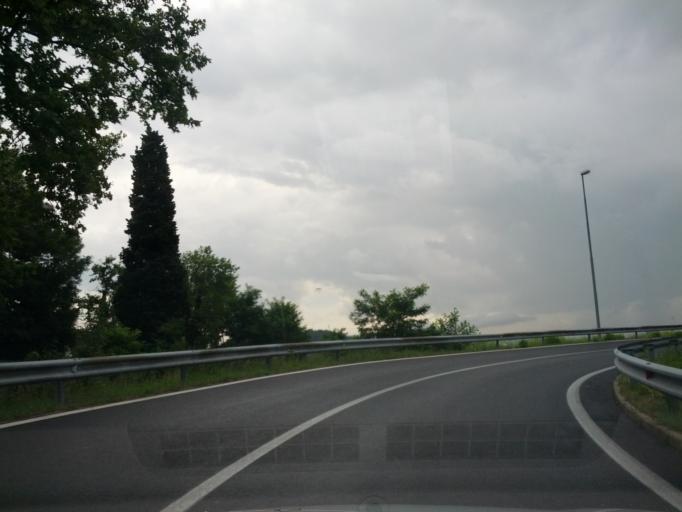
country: SI
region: Koper-Capodistria
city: Spodnje Skofije
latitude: 45.5654
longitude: 13.7856
